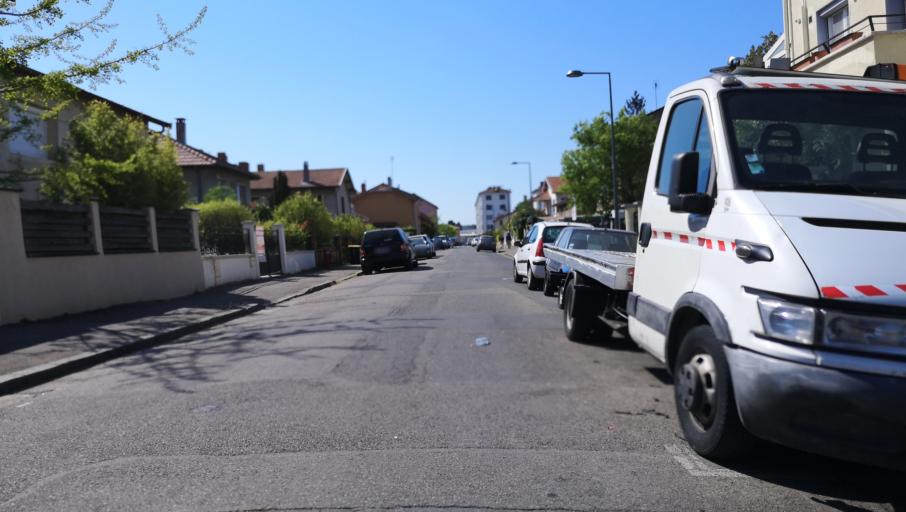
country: FR
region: Rhone-Alpes
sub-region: Departement du Rhone
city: Bron
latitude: 45.7522
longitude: 4.9180
